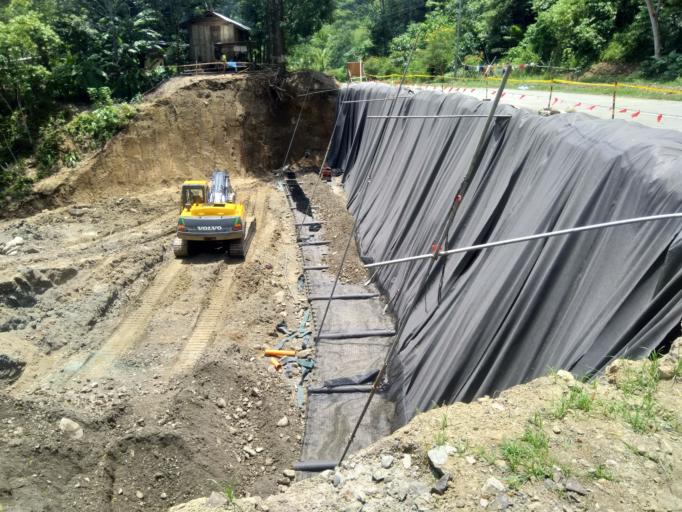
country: PH
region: Davao
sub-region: Province of Davao del Norte
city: Santo Nino
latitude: 7.6327
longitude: 125.5519
